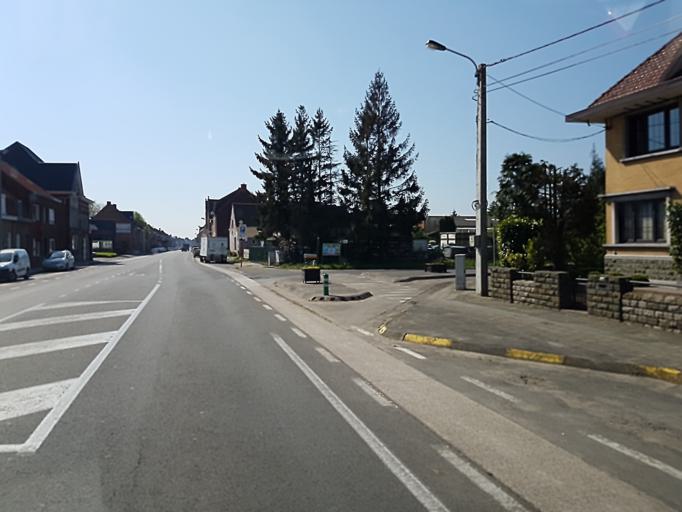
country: BE
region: Flanders
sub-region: Provincie West-Vlaanderen
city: Menen
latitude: 50.8117
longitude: 3.1213
